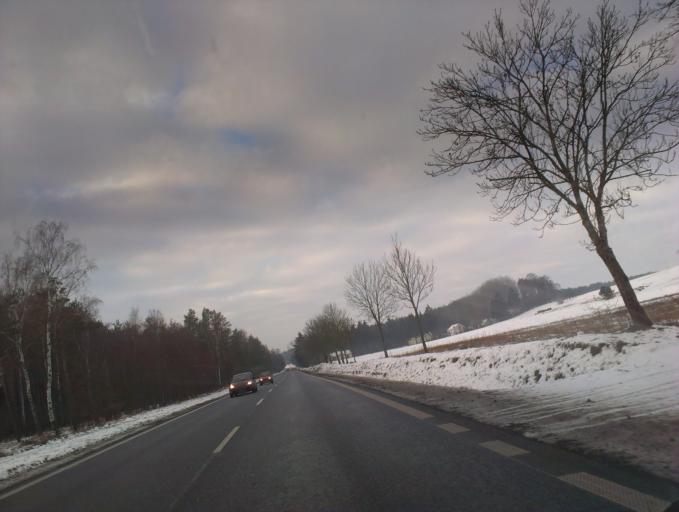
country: PL
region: Greater Poland Voivodeship
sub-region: Powiat zlotowski
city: Jastrowie
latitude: 53.4654
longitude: 16.8638
